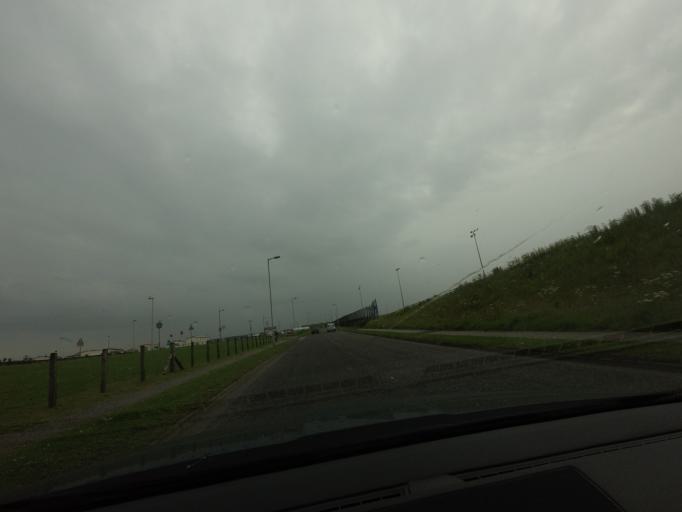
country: GB
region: Scotland
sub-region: Aberdeenshire
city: Fraserburgh
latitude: 57.6871
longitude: -2.0017
